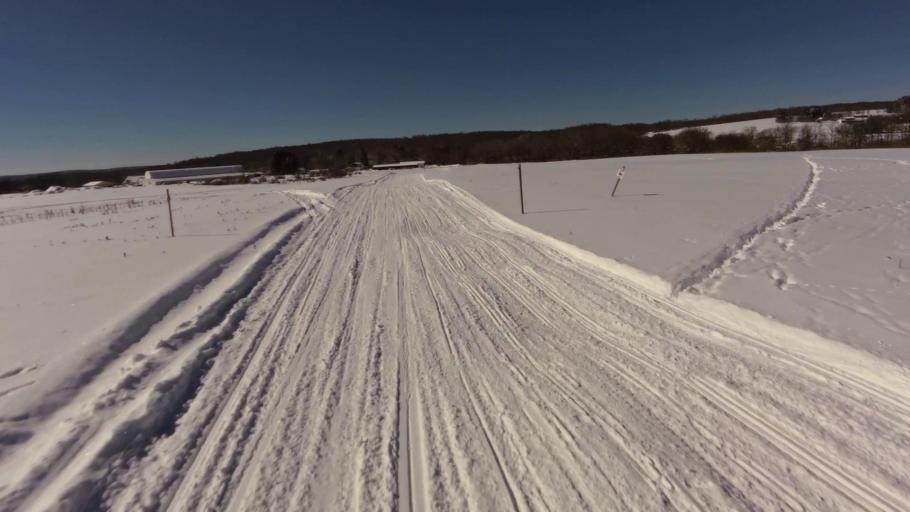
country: US
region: New York
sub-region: Chautauqua County
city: Mayville
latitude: 42.2478
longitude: -79.4312
